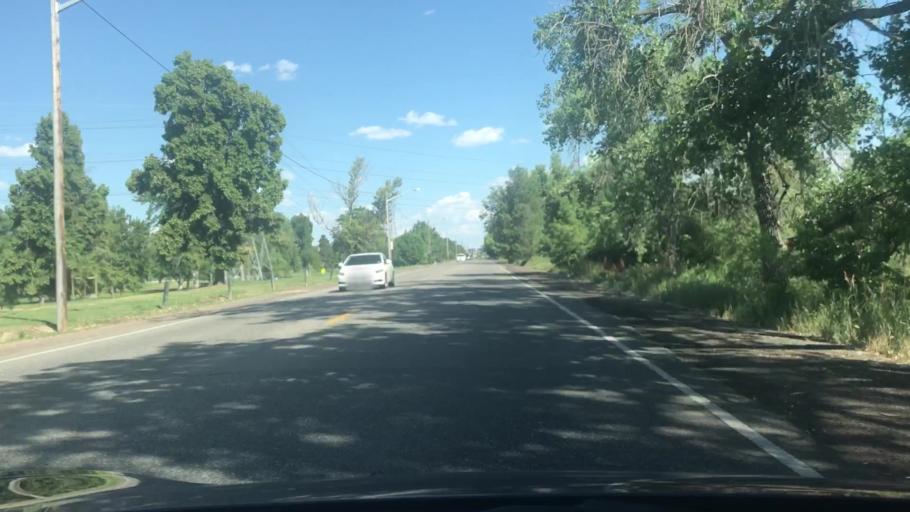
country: US
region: Colorado
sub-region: Arapahoe County
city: Glendale
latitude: 39.6950
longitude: -104.9193
